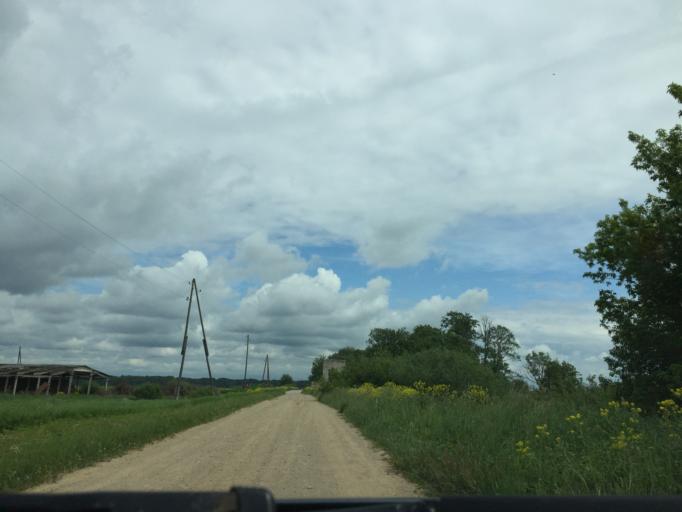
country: LV
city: Tireli
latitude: 56.6864
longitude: 23.5145
